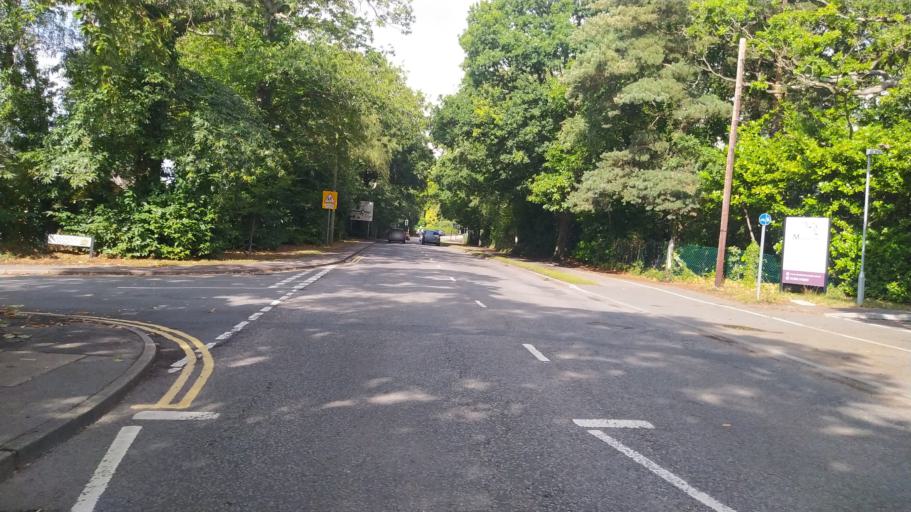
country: GB
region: England
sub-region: Poole
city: Canford Heath
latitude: 50.7500
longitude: -1.9807
